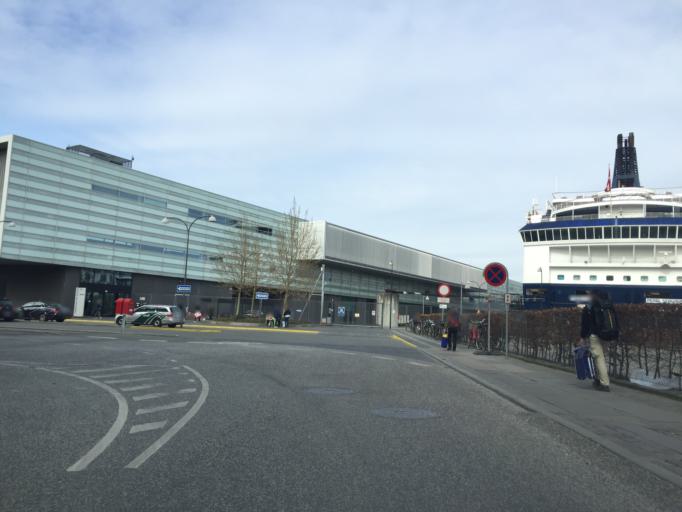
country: DK
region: Capital Region
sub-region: Kobenhavn
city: Christianshavn
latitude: 55.7005
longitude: 12.5955
